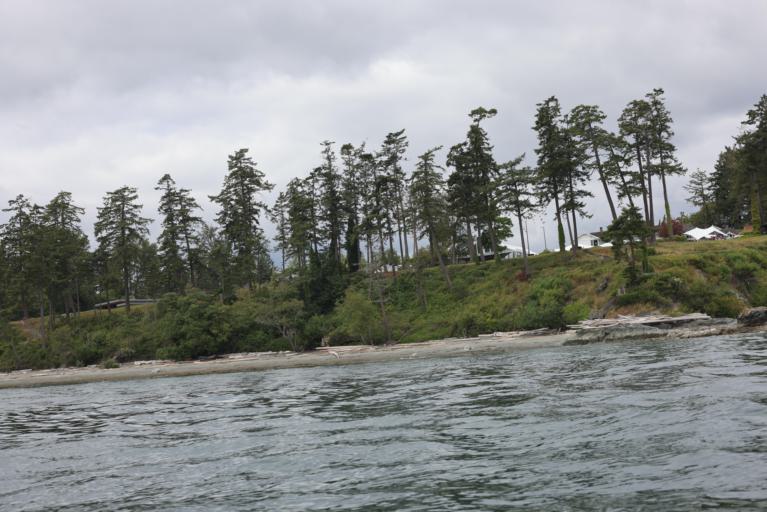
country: CA
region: British Columbia
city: Oak Bay
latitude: 48.5422
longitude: -123.3596
